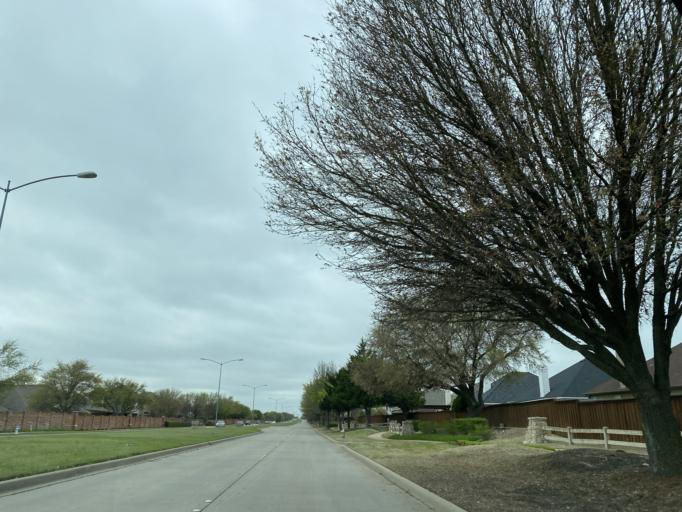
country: US
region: Texas
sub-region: Collin County
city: Fairview
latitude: 33.1269
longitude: -96.6287
